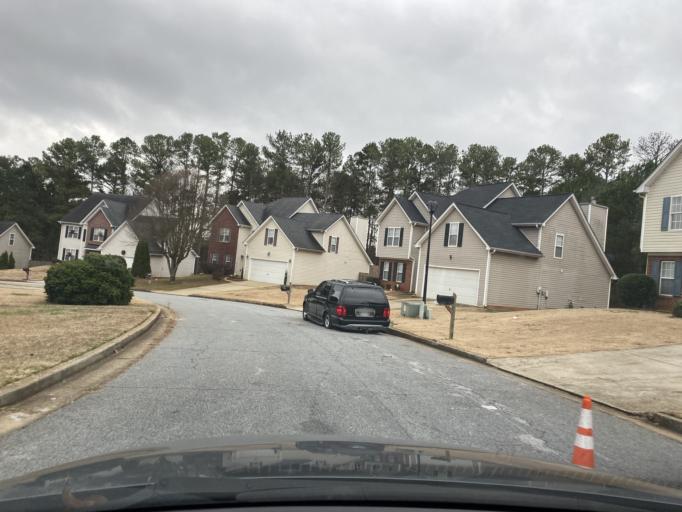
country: US
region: Georgia
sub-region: DeKalb County
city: Pine Mountain
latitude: 33.6976
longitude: -84.1649
